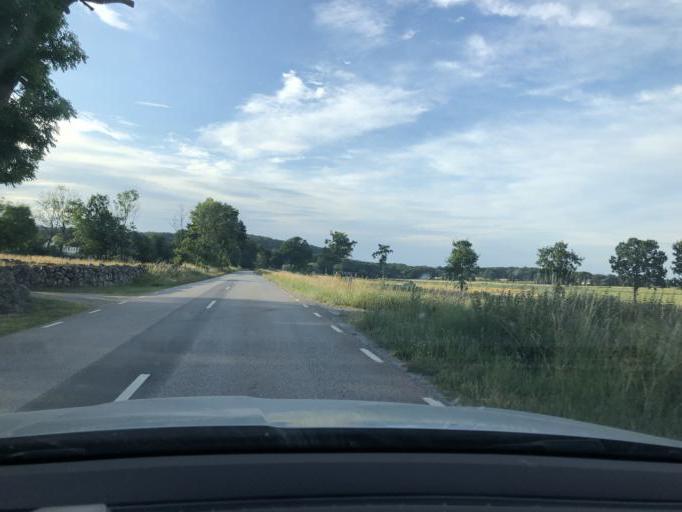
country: SE
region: Blekinge
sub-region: Solvesborgs Kommun
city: Soelvesborg
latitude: 56.0841
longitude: 14.6071
